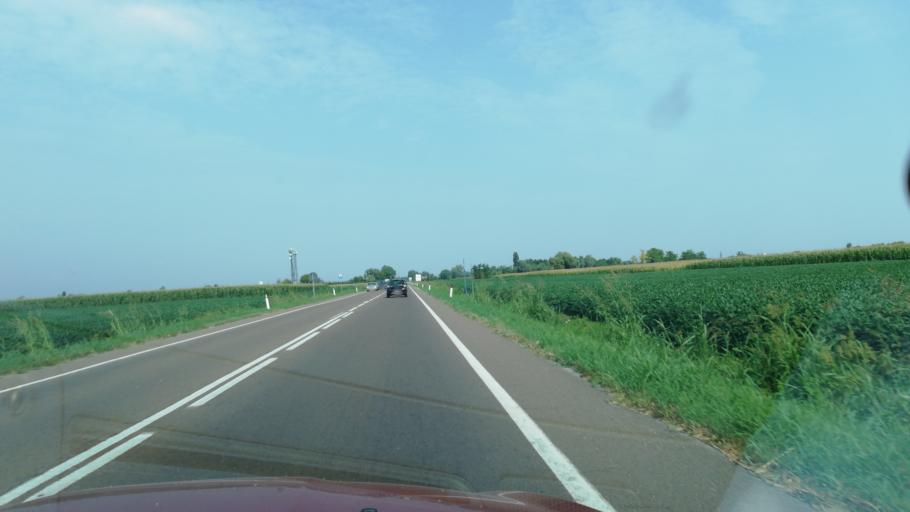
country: IT
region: Veneto
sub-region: Provincia di Venezia
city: San Michele al Tagliamento
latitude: 45.7515
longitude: 12.9892
